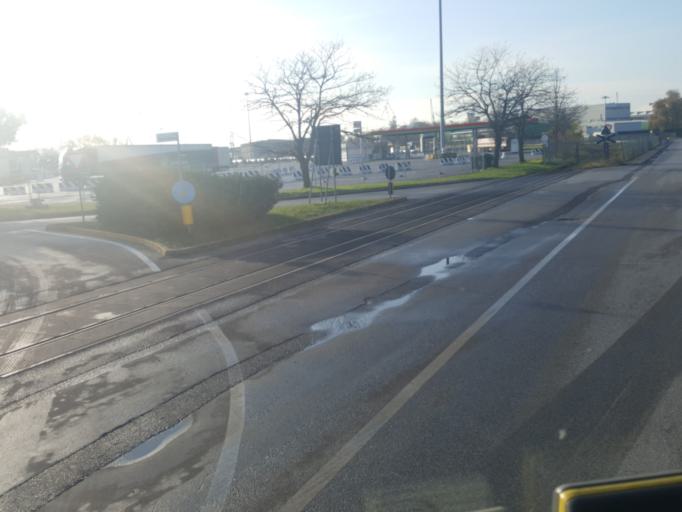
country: IT
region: Friuli Venezia Giulia
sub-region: Provincia di Gorizia
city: Monfalcone
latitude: 45.7924
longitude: 13.5620
